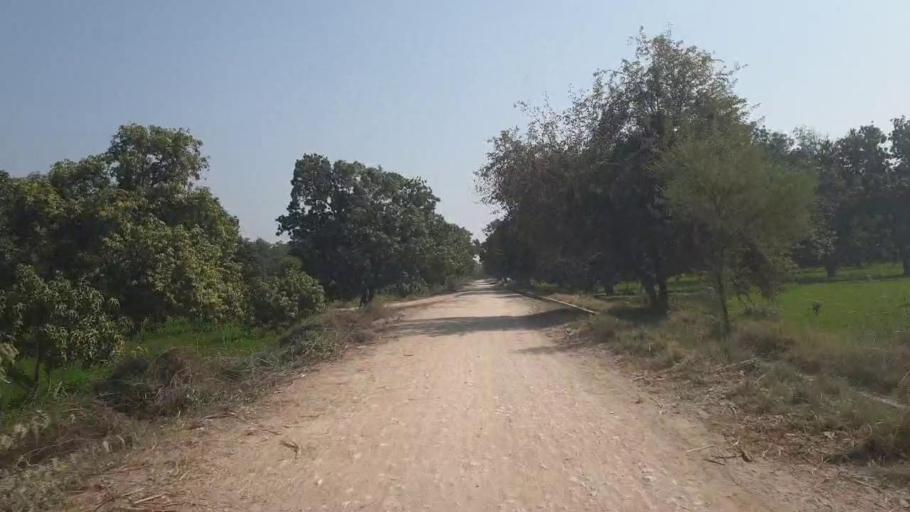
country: PK
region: Sindh
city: Tando Allahyar
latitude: 25.4336
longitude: 68.8473
